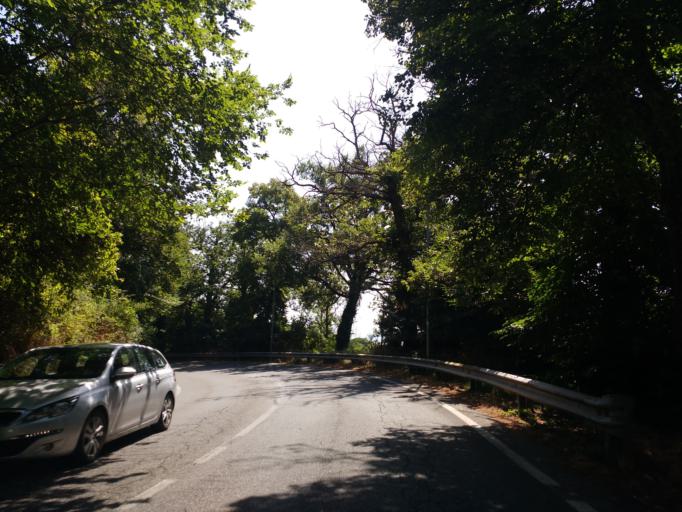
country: IT
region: Latium
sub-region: Citta metropolitana di Roma Capitale
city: Rocca di Papa
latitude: 41.7521
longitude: 12.7002
